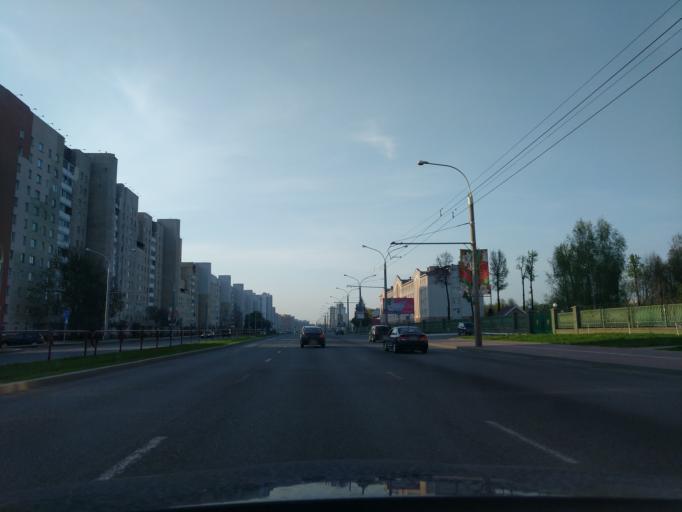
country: BY
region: Minsk
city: Minsk
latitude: 53.8658
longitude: 27.5709
